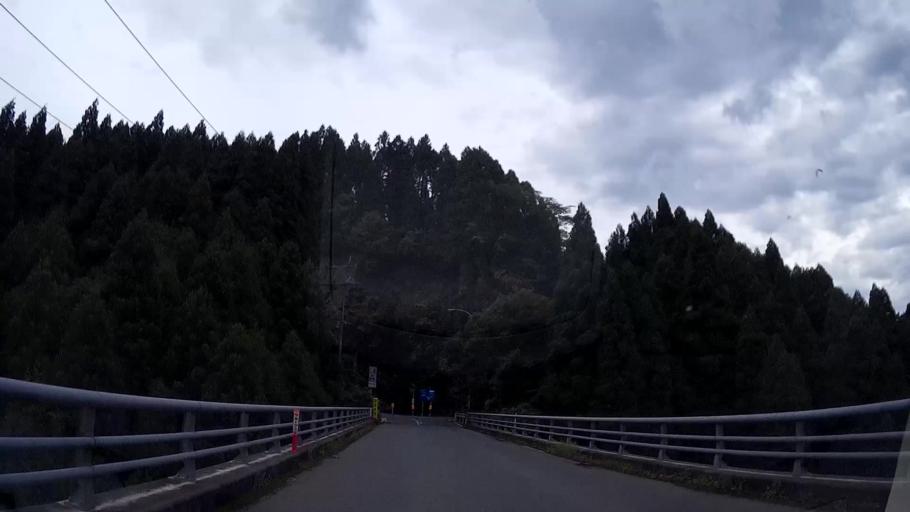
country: JP
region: Oita
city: Hita
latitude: 33.1377
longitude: 130.9774
